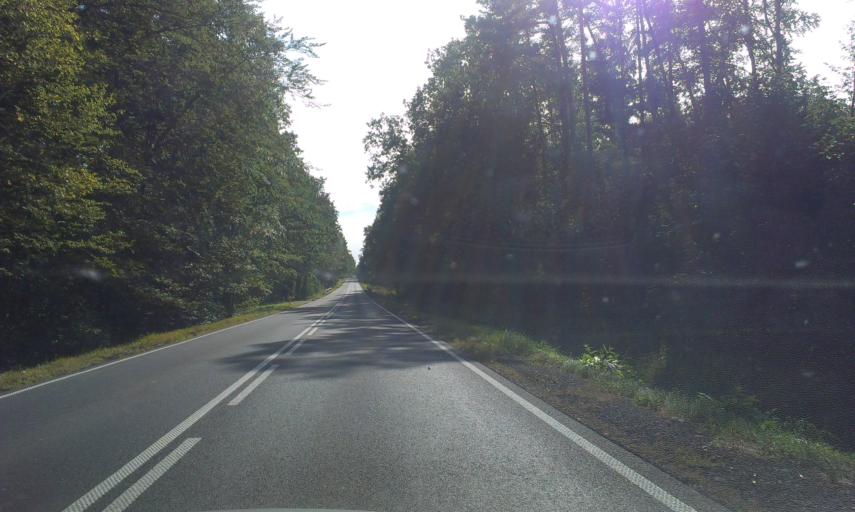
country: PL
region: West Pomeranian Voivodeship
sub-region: Powiat szczecinecki
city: Szczecinek
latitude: 53.6362
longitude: 16.7643
